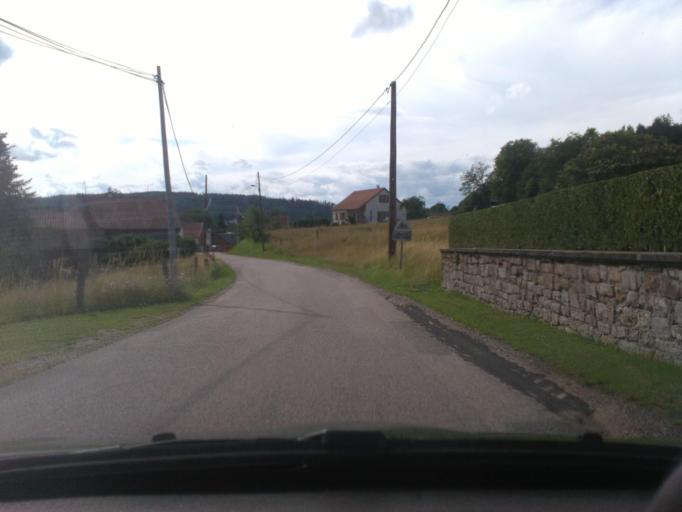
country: FR
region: Lorraine
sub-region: Departement des Vosges
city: Bruyeres
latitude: 48.2345
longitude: 6.7549
